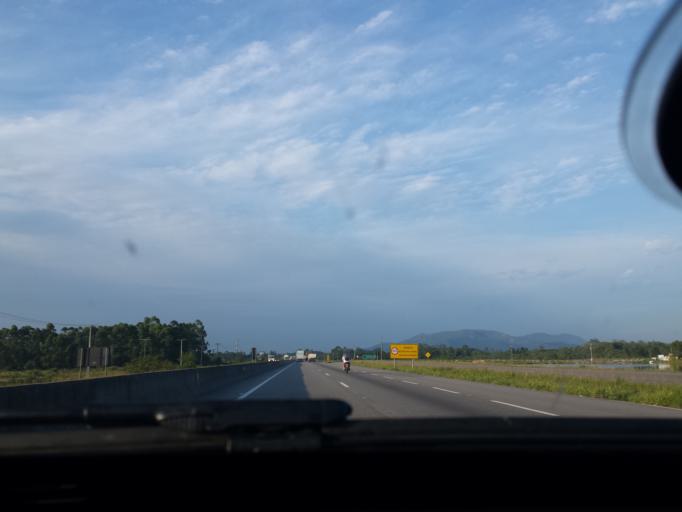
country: BR
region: Santa Catarina
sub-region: Laguna
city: Laguna
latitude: -28.3957
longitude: -48.7817
